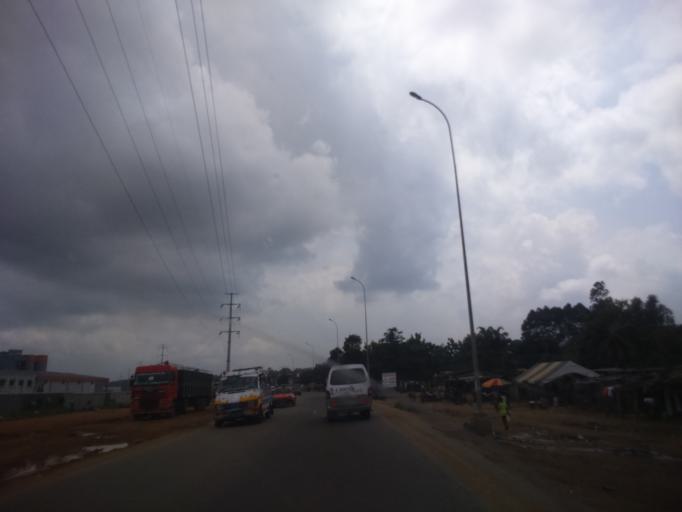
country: CI
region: Lagunes
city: Abobo
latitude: 5.3823
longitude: -4.0756
